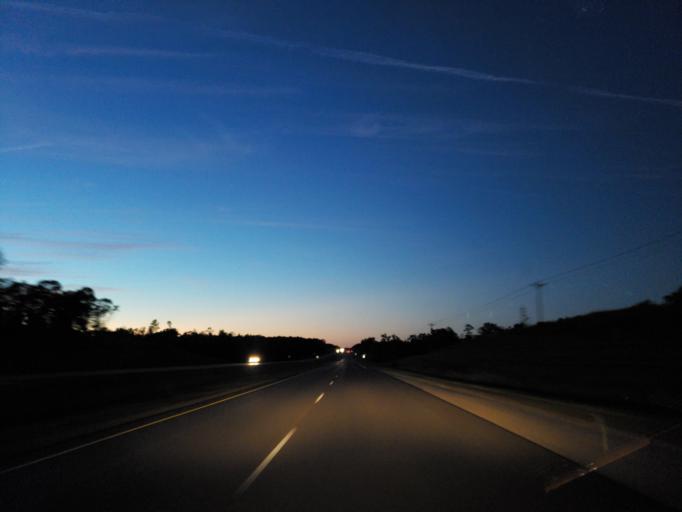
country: US
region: Mississippi
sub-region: Clarke County
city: Quitman
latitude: 32.0661
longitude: -88.6816
